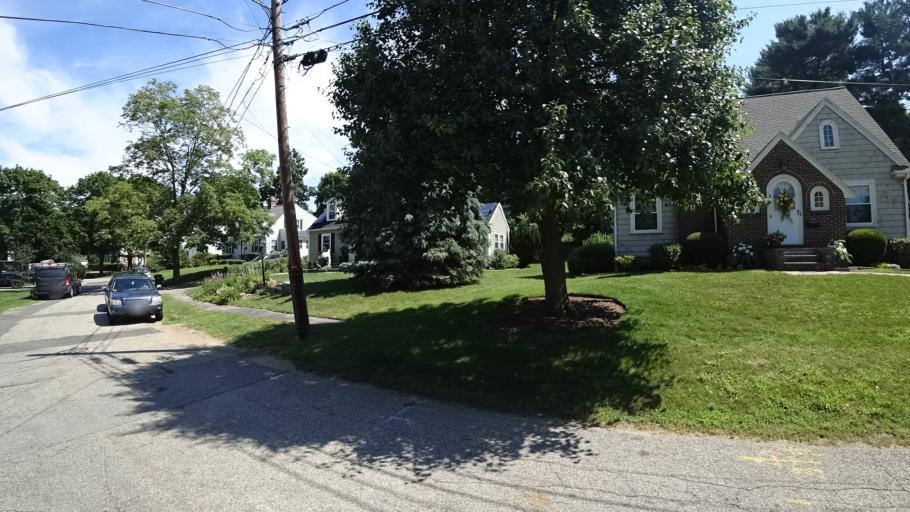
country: US
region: Massachusetts
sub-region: Norfolk County
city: Dedham
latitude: 42.2373
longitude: -71.1649
